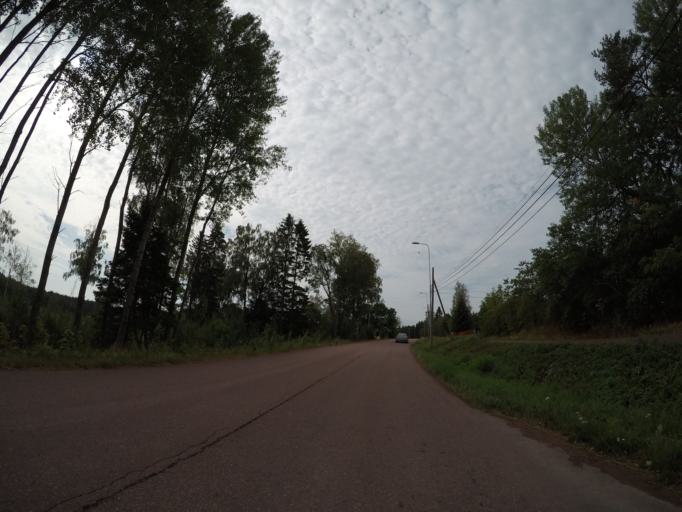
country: AX
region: Alands landsbygd
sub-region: Finstroem
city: Finstroem
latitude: 60.2195
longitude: 19.9806
